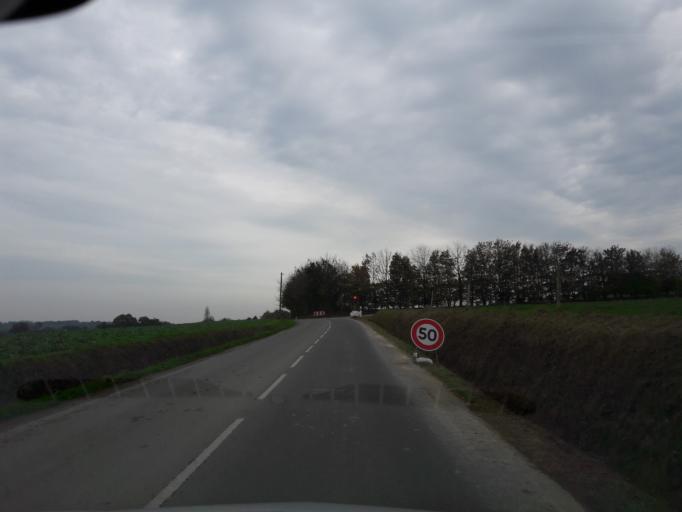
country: FR
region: Brittany
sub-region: Departement d'Ille-et-Vilaine
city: Le Theil-de-Bretagne
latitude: 47.9596
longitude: -1.4318
